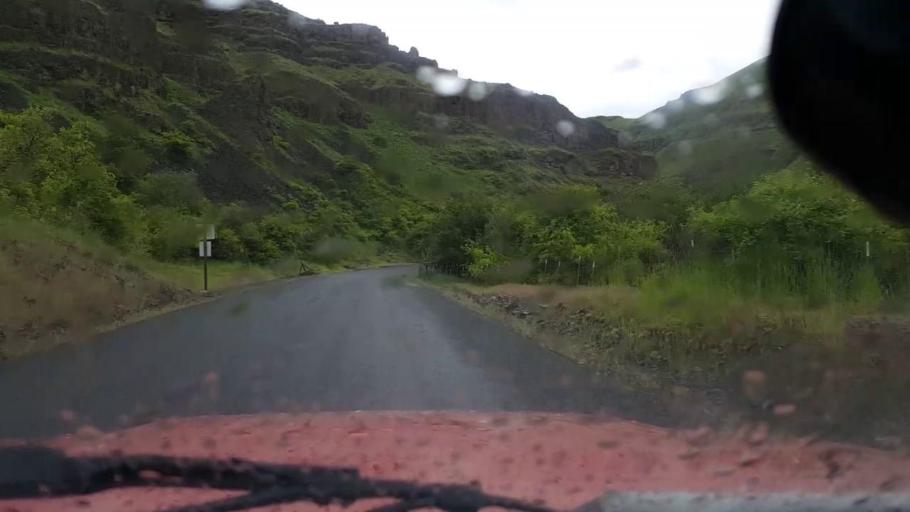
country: US
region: Washington
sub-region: Asotin County
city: Asotin
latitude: 46.0434
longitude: -117.2566
